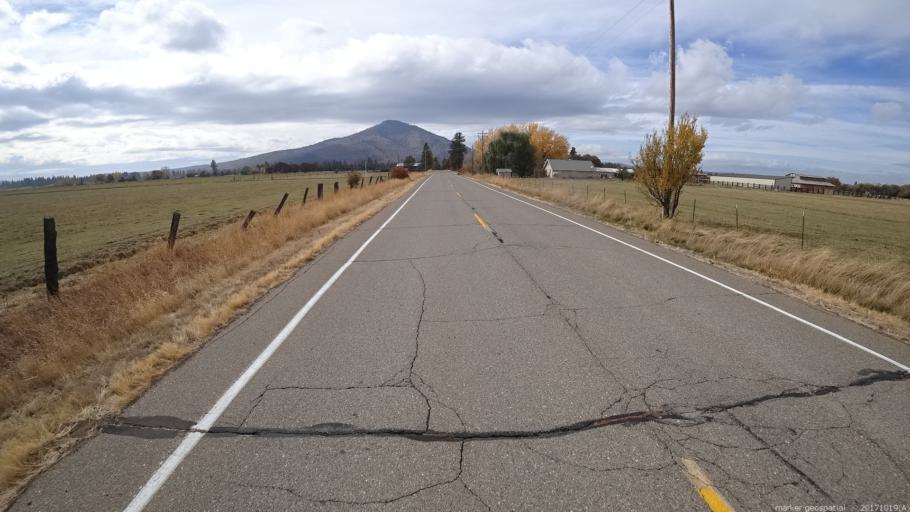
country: US
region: California
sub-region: Shasta County
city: Burney
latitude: 41.0798
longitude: -121.5032
